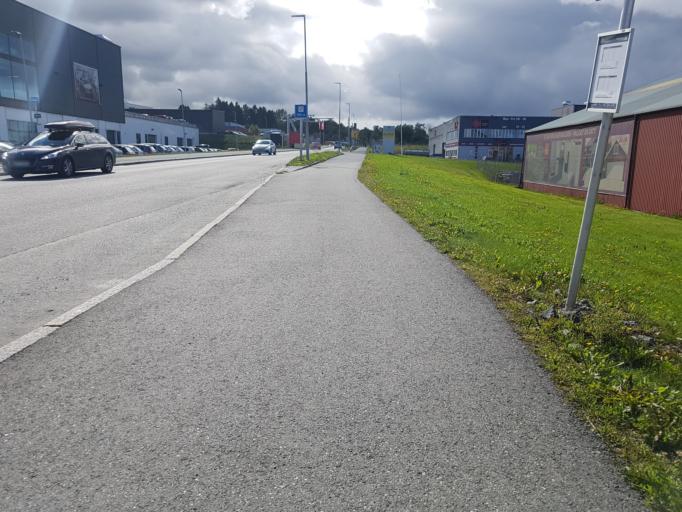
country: NO
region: Sor-Trondelag
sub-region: Trondheim
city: Trondheim
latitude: 63.4231
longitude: 10.4639
